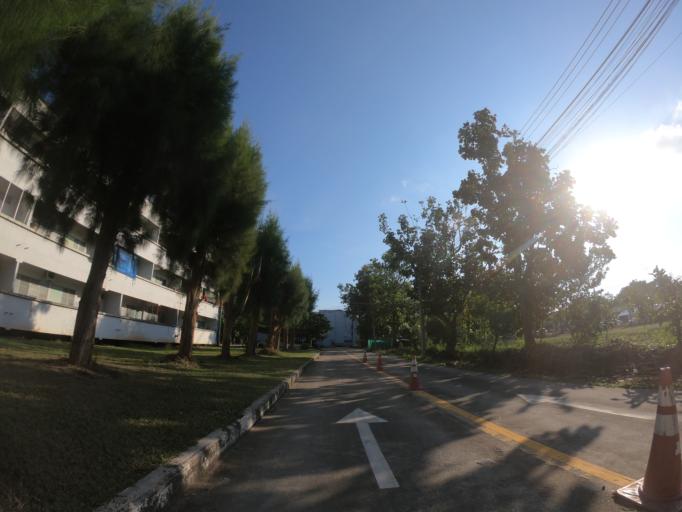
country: TH
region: Chiang Mai
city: Chiang Mai
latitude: 18.7453
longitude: 98.9632
